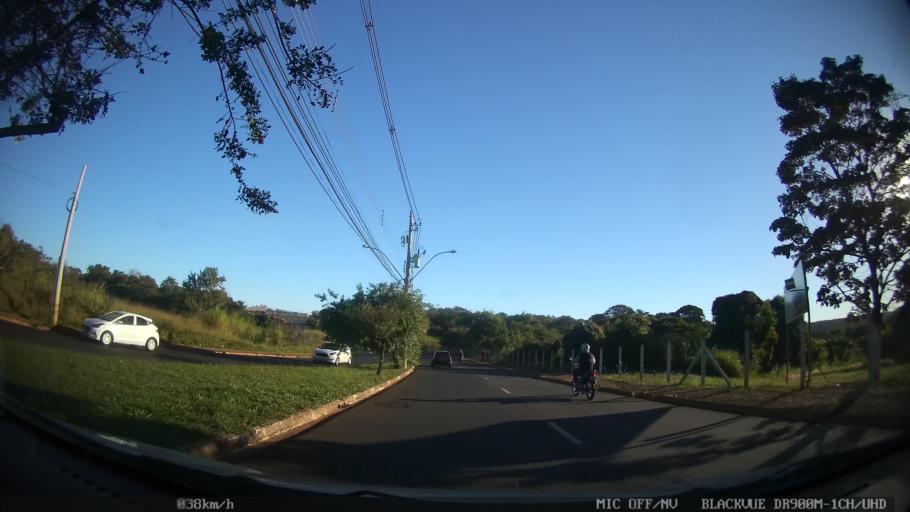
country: BR
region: Sao Paulo
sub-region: Araraquara
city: Araraquara
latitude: -21.7467
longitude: -48.1609
